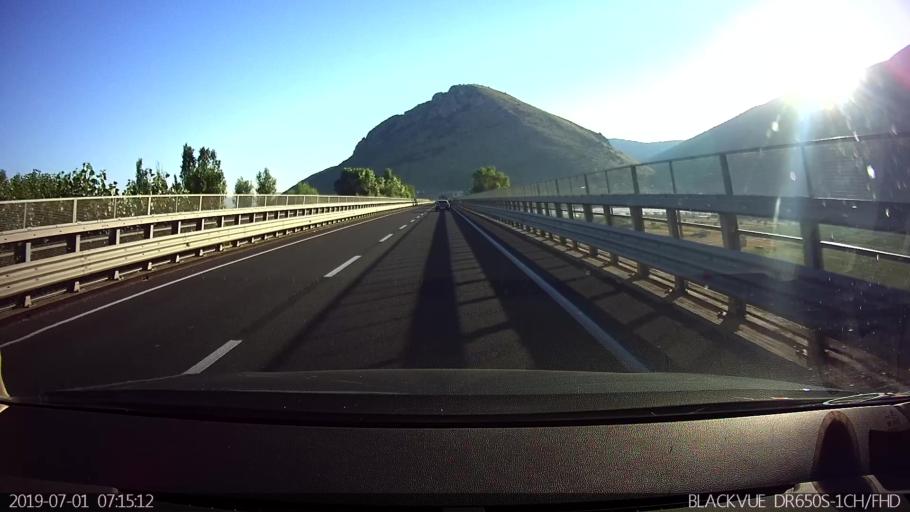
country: IT
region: Latium
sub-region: Provincia di Latina
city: Borgo Hermada
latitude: 41.3297
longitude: 13.1912
